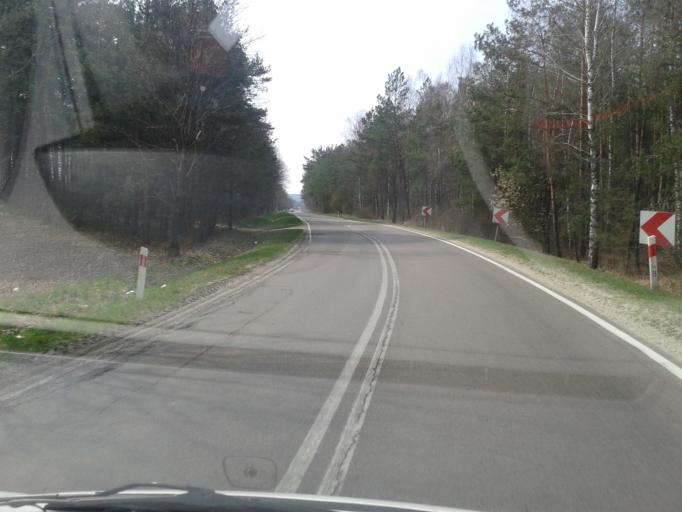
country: PL
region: Subcarpathian Voivodeship
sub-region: Powiat lubaczowski
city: Narol
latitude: 50.3639
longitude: 23.3438
